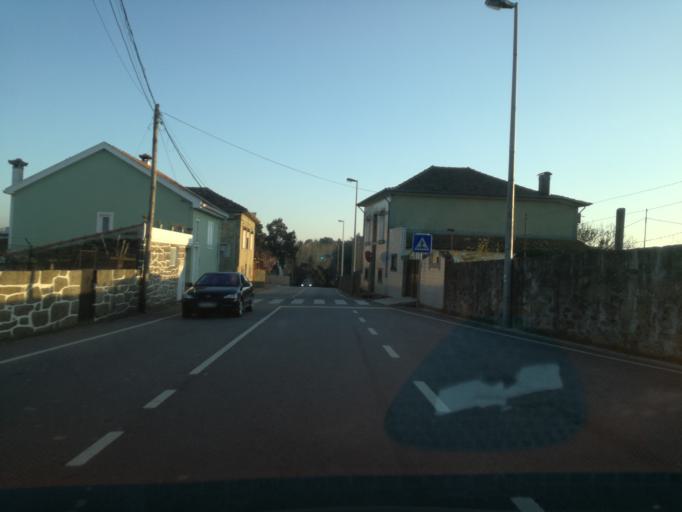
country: PT
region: Porto
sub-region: Maia
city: Milheiros
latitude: 41.2189
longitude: -8.5979
